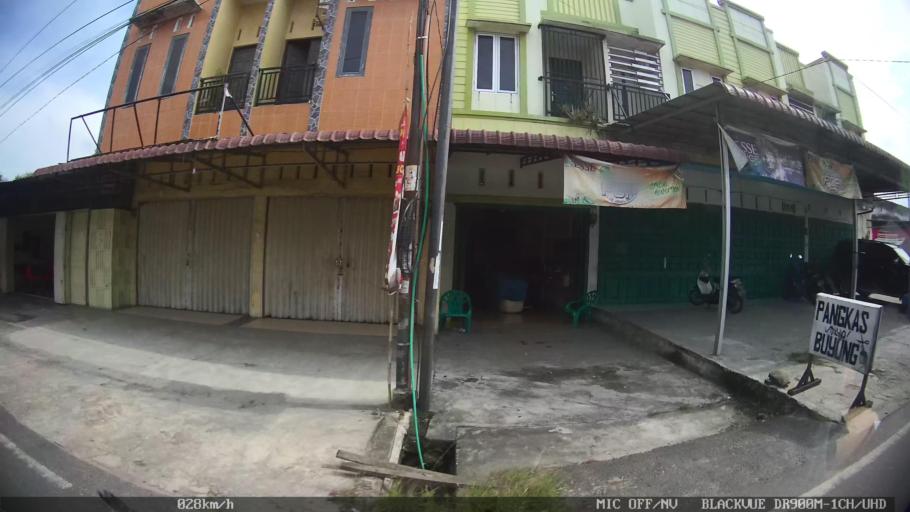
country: ID
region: North Sumatra
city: Percut
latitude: 3.6071
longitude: 98.7677
